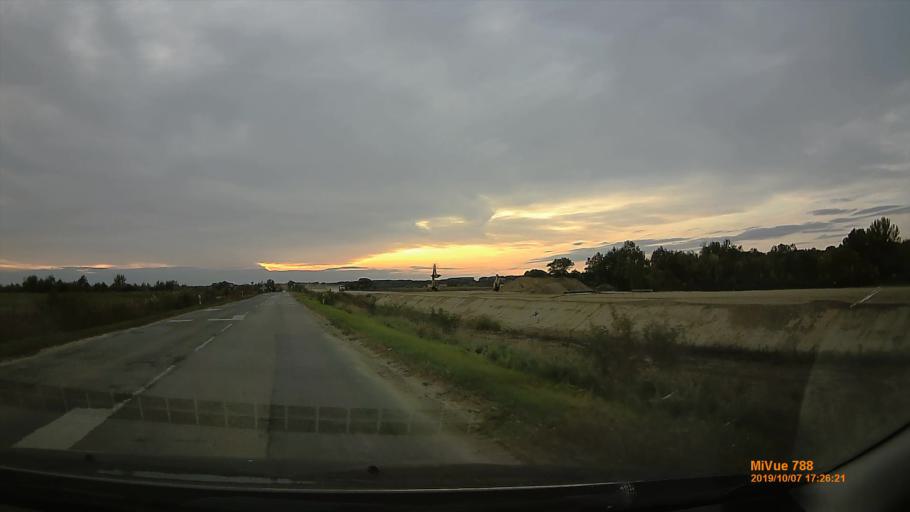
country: HU
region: Bacs-Kiskun
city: Tiszakecske
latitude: 46.8687
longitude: 20.0930
